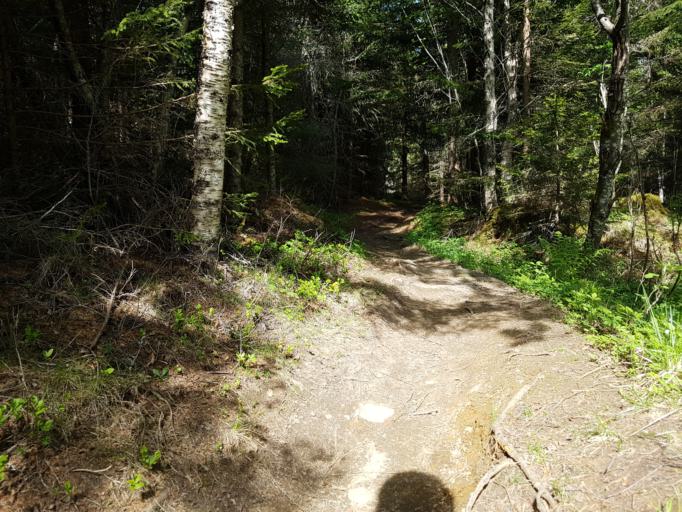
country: NO
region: Sor-Trondelag
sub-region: Trondheim
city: Trondheim
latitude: 63.4277
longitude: 10.3338
